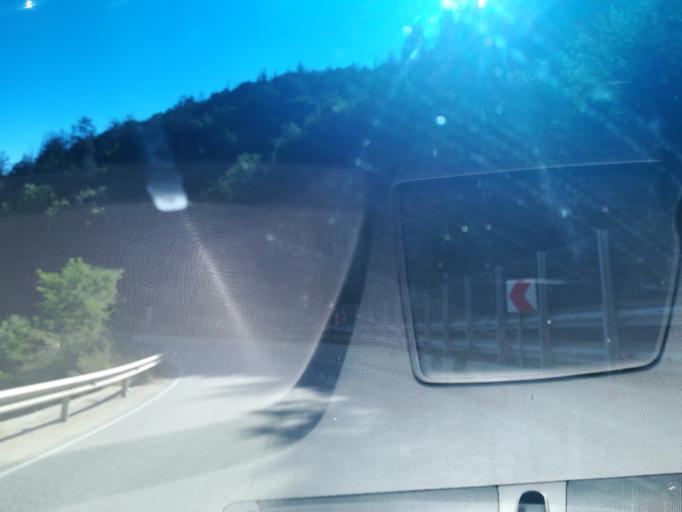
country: BG
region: Plovdiv
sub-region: Obshtina Luki
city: Luki
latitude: 41.9069
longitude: 24.7623
